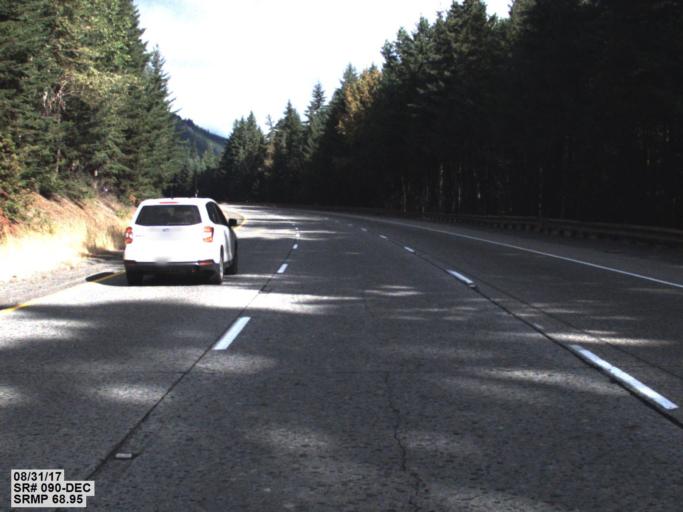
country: US
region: Washington
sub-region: Kittitas County
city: Cle Elum
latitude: 47.2608
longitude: -121.2112
